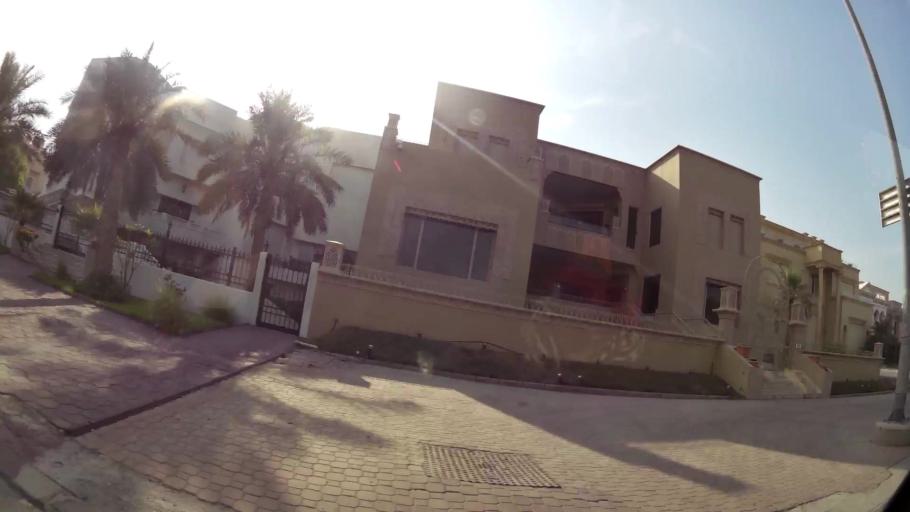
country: KW
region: Al Asimah
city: Ash Shamiyah
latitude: 29.3255
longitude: 47.9812
